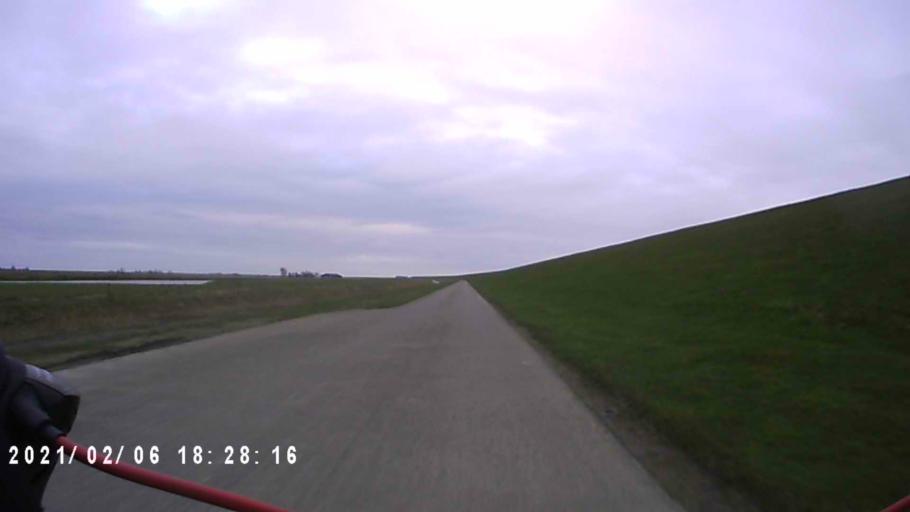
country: DE
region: Lower Saxony
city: Borkum
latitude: 53.4597
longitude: 6.6863
